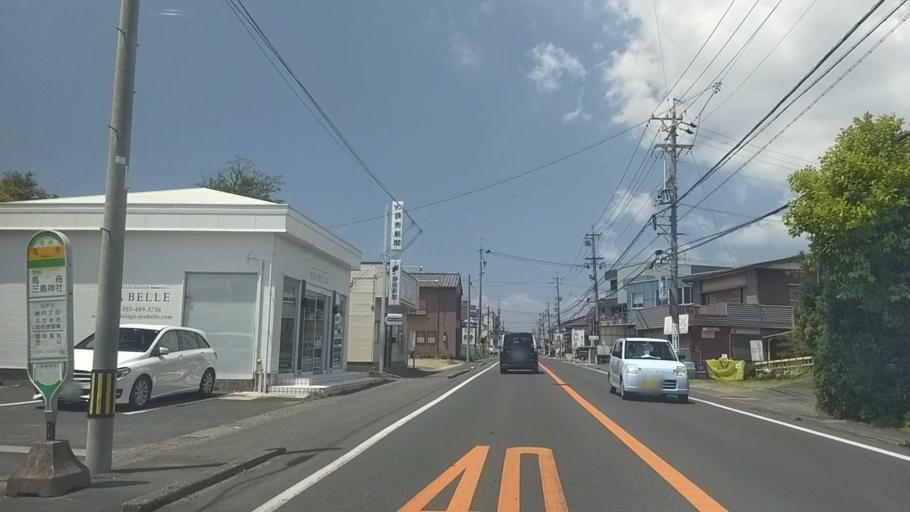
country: JP
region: Shizuoka
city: Hamamatsu
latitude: 34.7370
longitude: 137.7164
